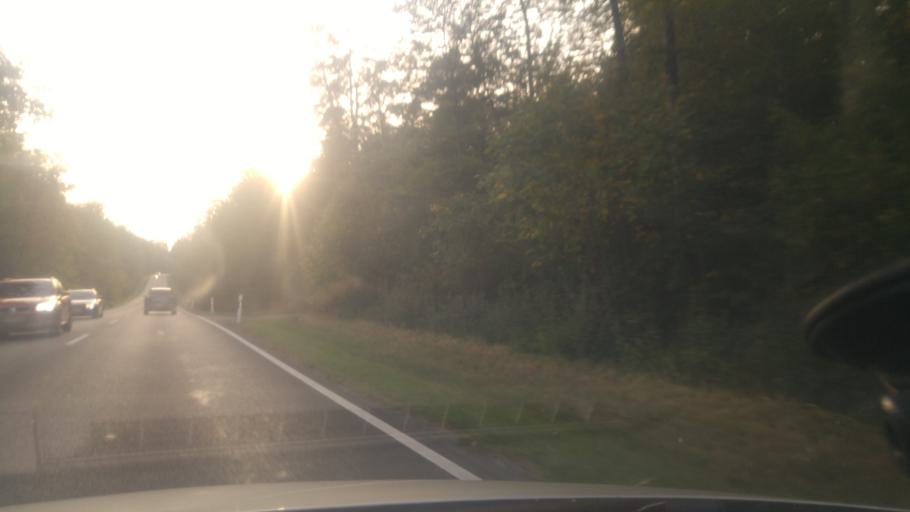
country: DE
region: Baden-Wuerttemberg
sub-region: Regierungsbezirk Stuttgart
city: Gerlingen
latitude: 48.7500
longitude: 9.0739
